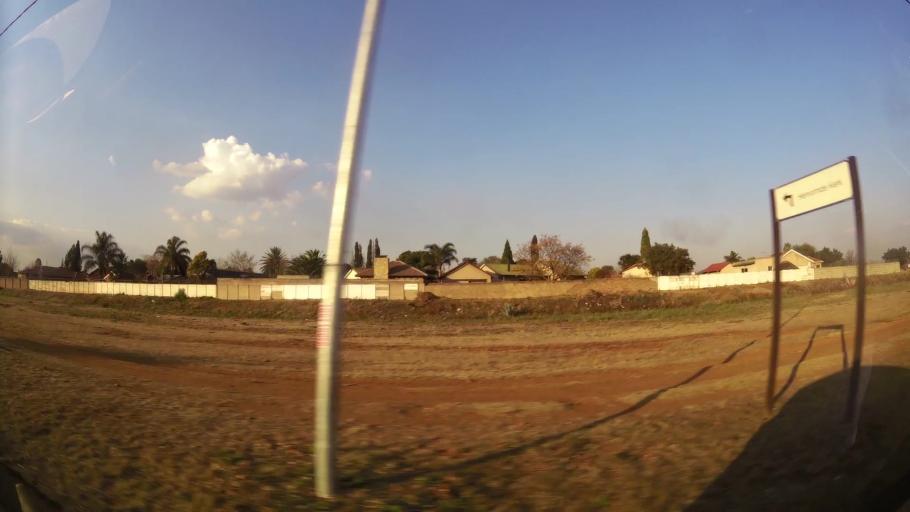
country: ZA
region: Gauteng
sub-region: Ekurhuleni Metropolitan Municipality
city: Germiston
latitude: -26.2839
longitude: 28.2273
